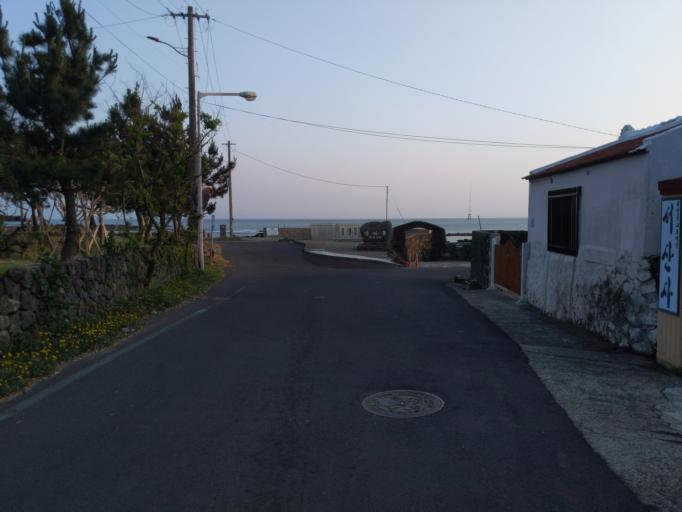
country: KR
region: Jeju-do
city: Gaigeturi
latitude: 33.2214
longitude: 126.2467
